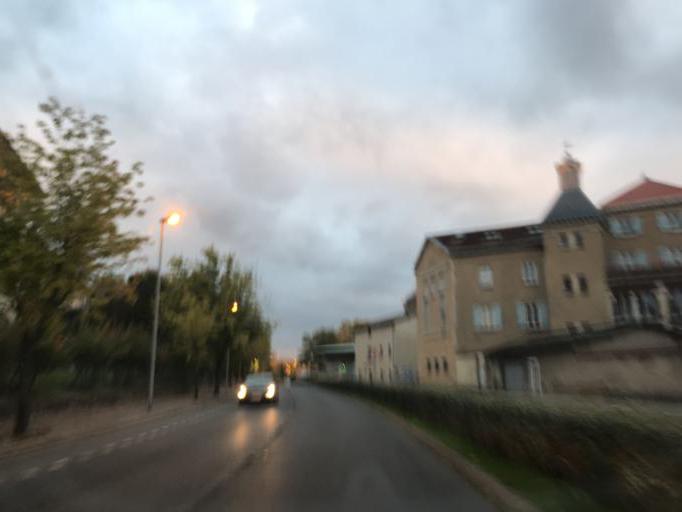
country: FR
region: Rhone-Alpes
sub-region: Departement de l'Ain
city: Saint-Didier-de-Formans
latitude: 45.9379
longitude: 4.7828
